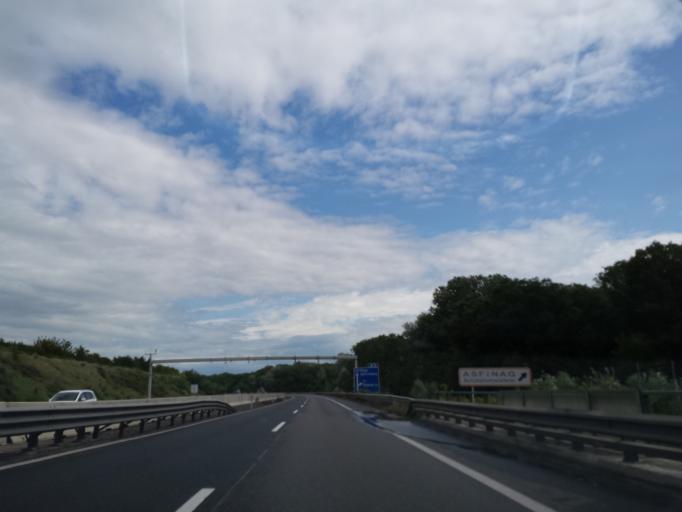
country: AT
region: Lower Austria
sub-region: Politischer Bezirk Korneuburg
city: Stockerau
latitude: 48.3781
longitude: 16.2228
